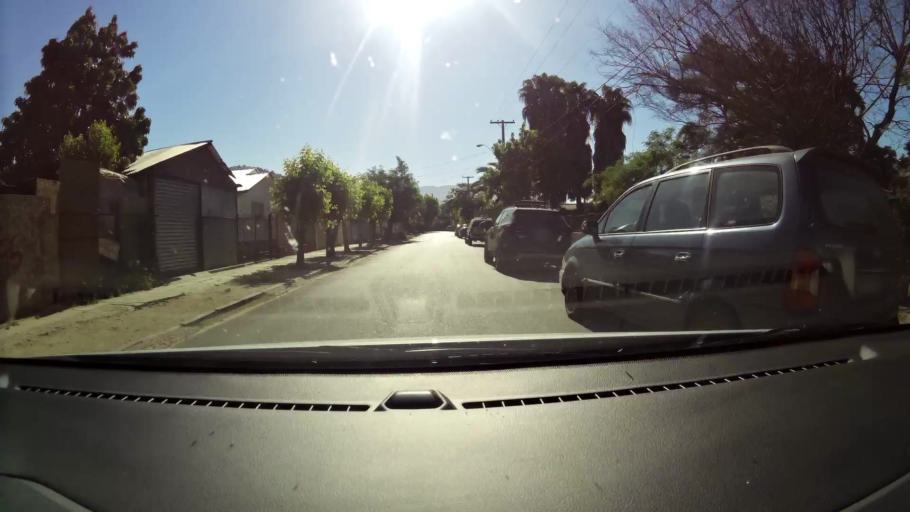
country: CL
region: Santiago Metropolitan
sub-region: Provincia de Chacabuco
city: Lampa
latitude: -33.4008
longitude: -71.1286
